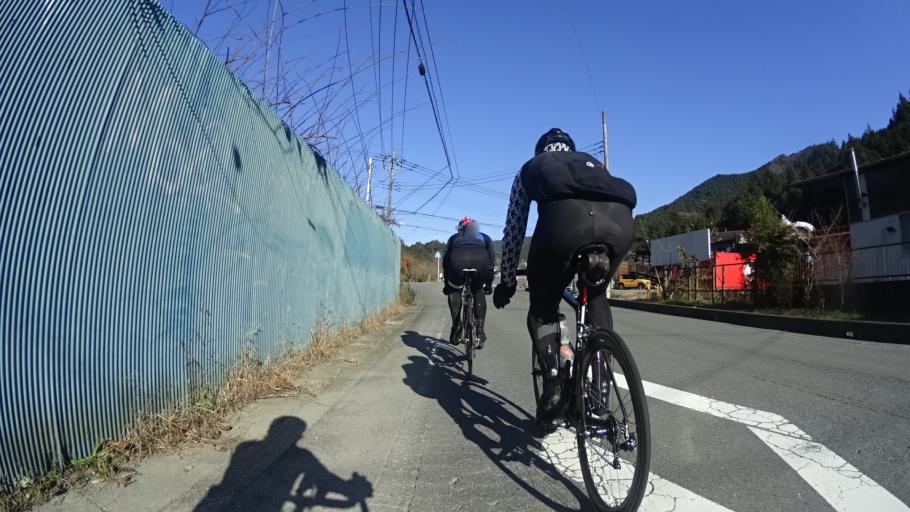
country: JP
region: Tokyo
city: Ome
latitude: 35.8650
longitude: 139.1868
